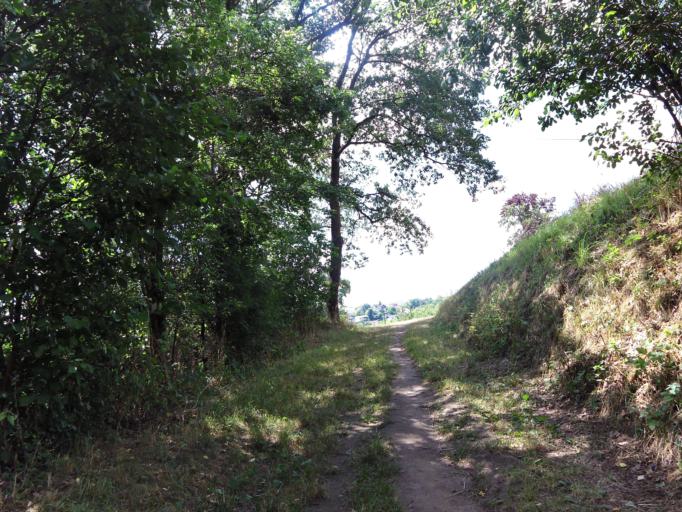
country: DE
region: Bavaria
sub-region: Regierungsbezirk Unterfranken
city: Gerbrunn
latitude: 49.7817
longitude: 9.9941
